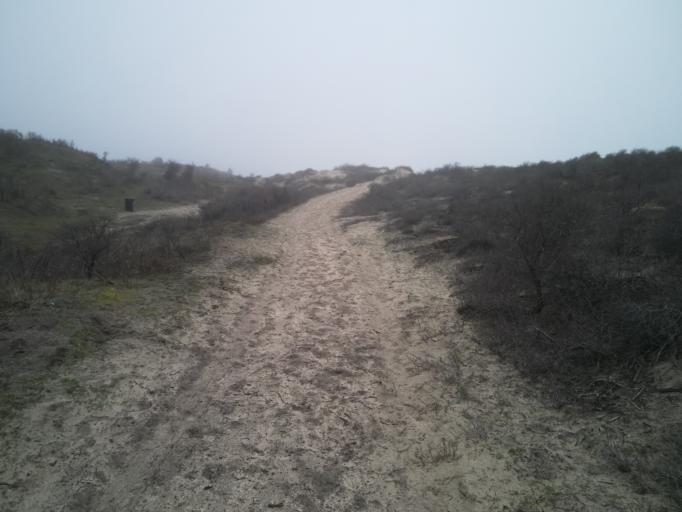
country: NL
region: South Holland
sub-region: Gemeente Noordwijkerhout
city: Noordwijkerhout
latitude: 52.3223
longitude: 4.4993
